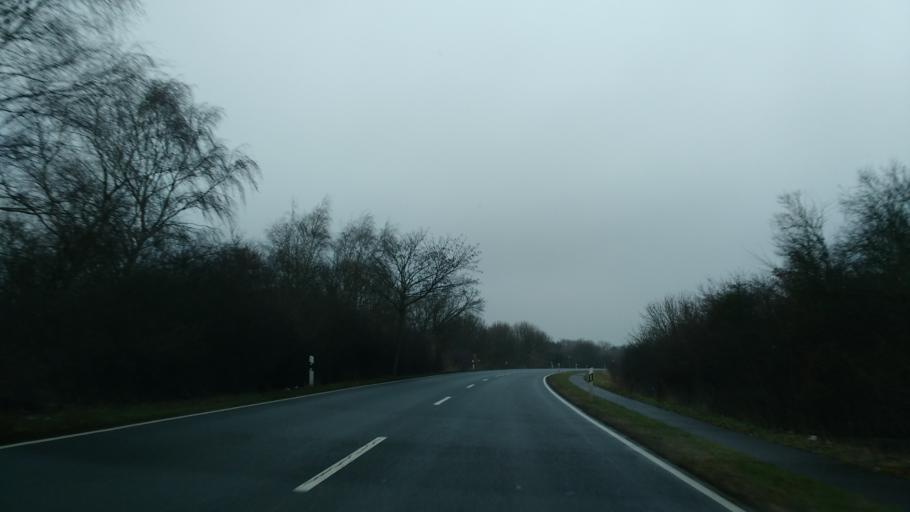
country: DE
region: Lower Saxony
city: Garbsen
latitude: 52.4293
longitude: 9.5723
